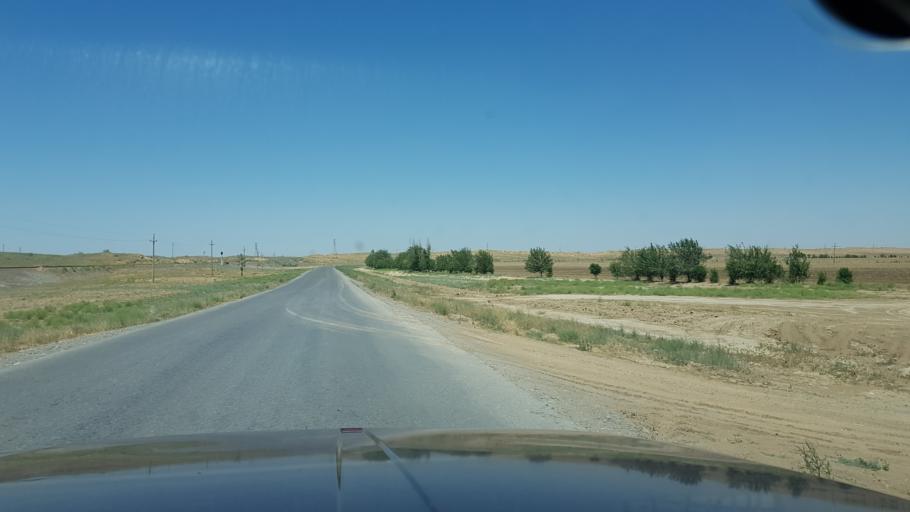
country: TM
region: Ahal
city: Annau
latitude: 37.8511
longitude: 58.7119
